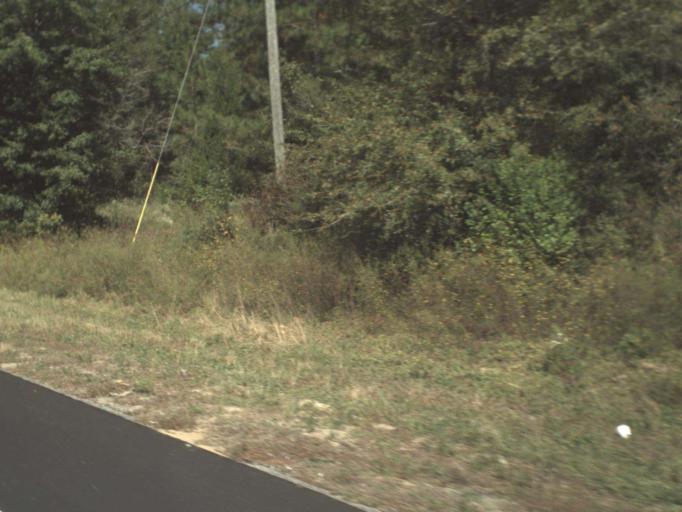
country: US
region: Florida
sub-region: Walton County
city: DeFuniak Springs
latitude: 30.7913
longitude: -86.1858
